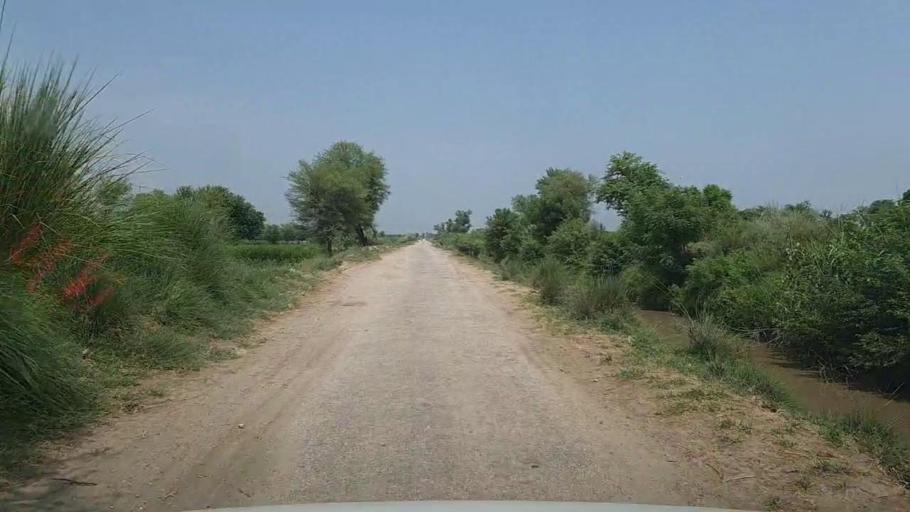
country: PK
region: Sindh
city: Karaundi
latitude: 26.8768
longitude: 68.3359
